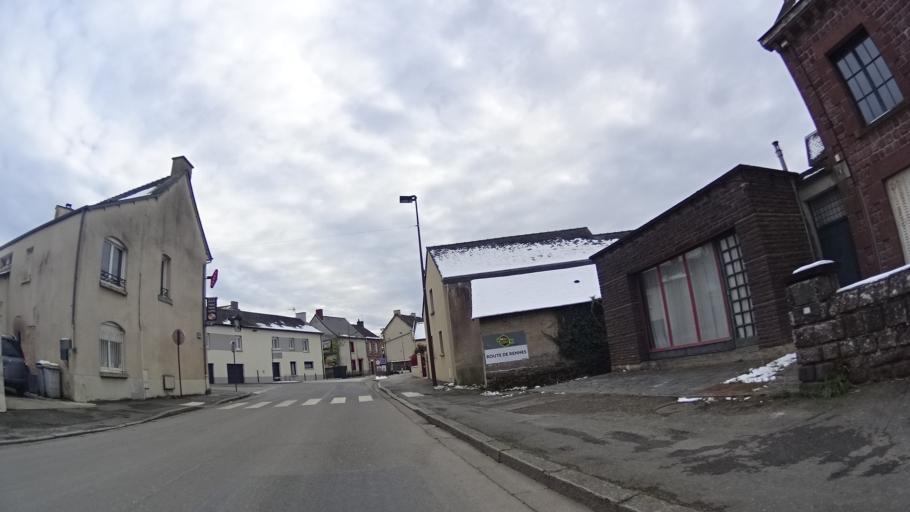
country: FR
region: Brittany
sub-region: Departement d'Ille-et-Vilaine
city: Montauban-de-Bretagne
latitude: 48.2025
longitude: -2.0465
